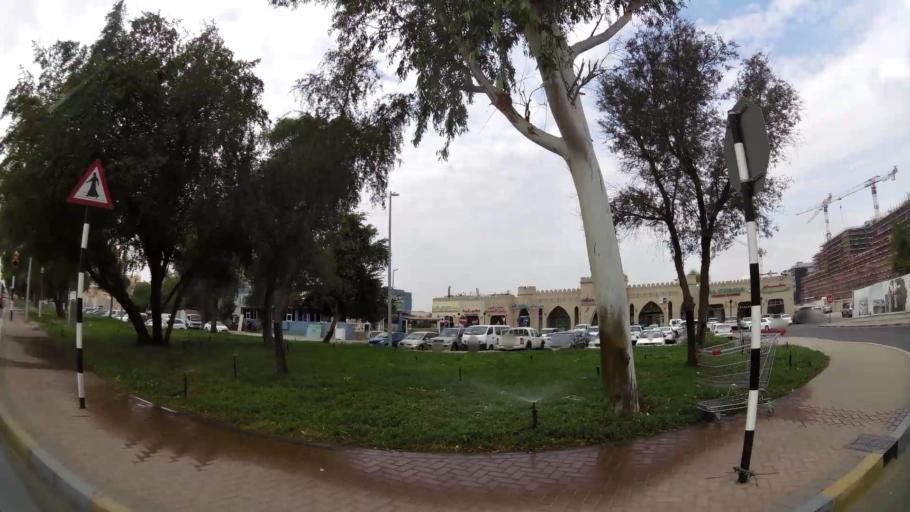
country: AE
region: Abu Dhabi
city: Al Ain
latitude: 24.2281
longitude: 55.7381
